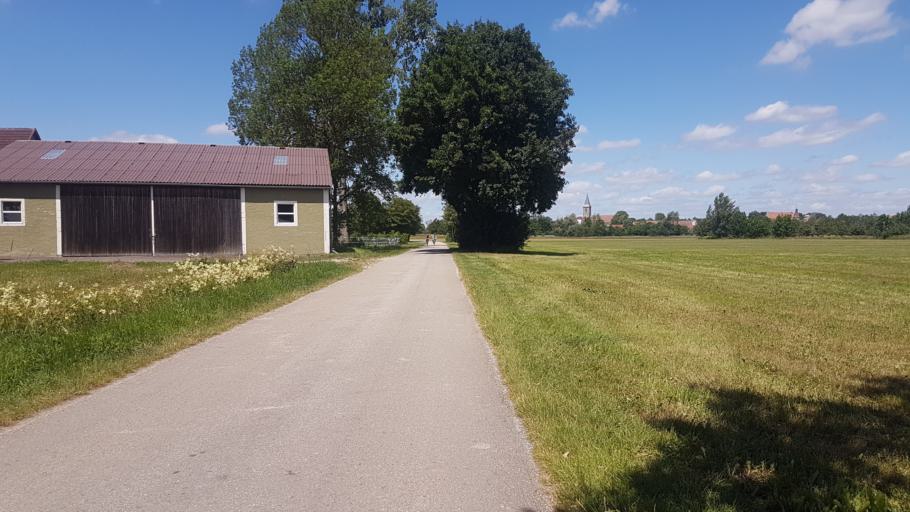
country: DE
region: Bavaria
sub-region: Regierungsbezirk Mittelfranken
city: Leutershausen
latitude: 49.2933
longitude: 10.4097
